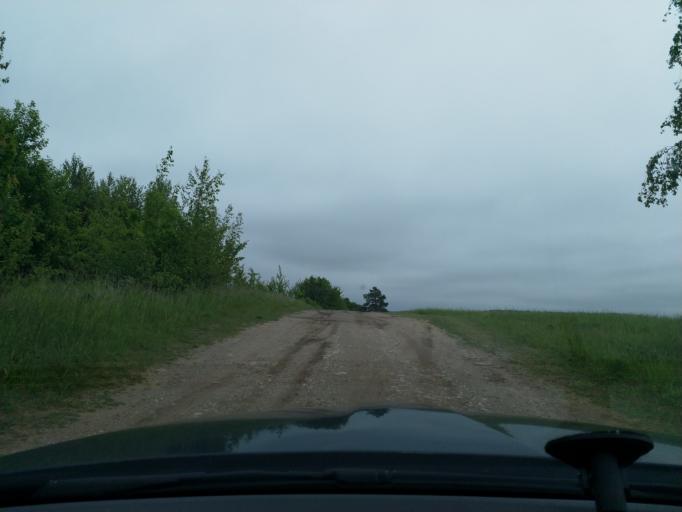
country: LV
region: Kuldigas Rajons
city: Kuldiga
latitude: 56.8791
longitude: 21.8244
